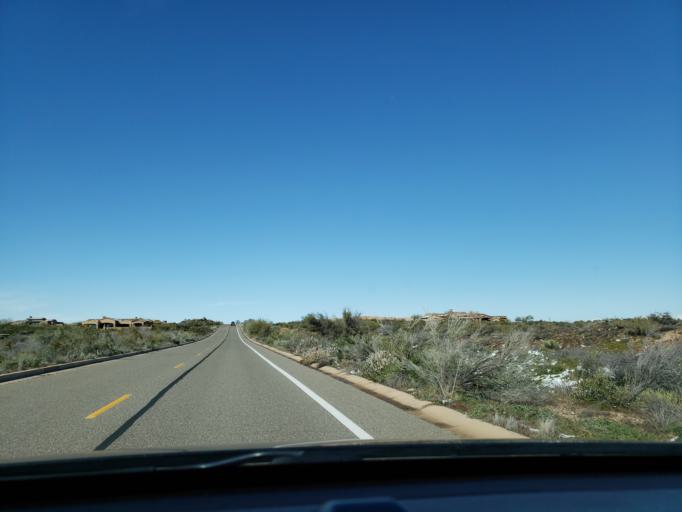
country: US
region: Arizona
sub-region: Maricopa County
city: Carefree
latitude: 33.7213
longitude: -111.8264
